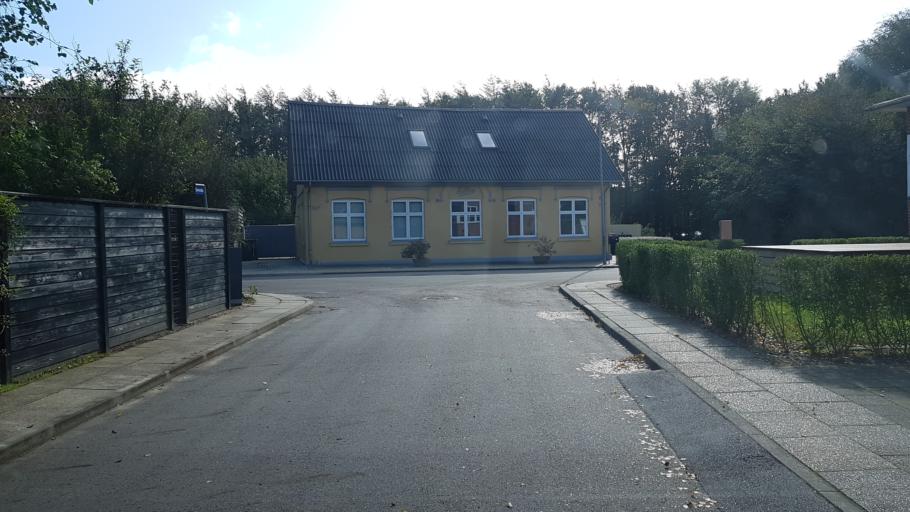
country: DK
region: South Denmark
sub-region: Varde Kommune
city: Olgod
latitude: 55.7154
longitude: 8.6003
